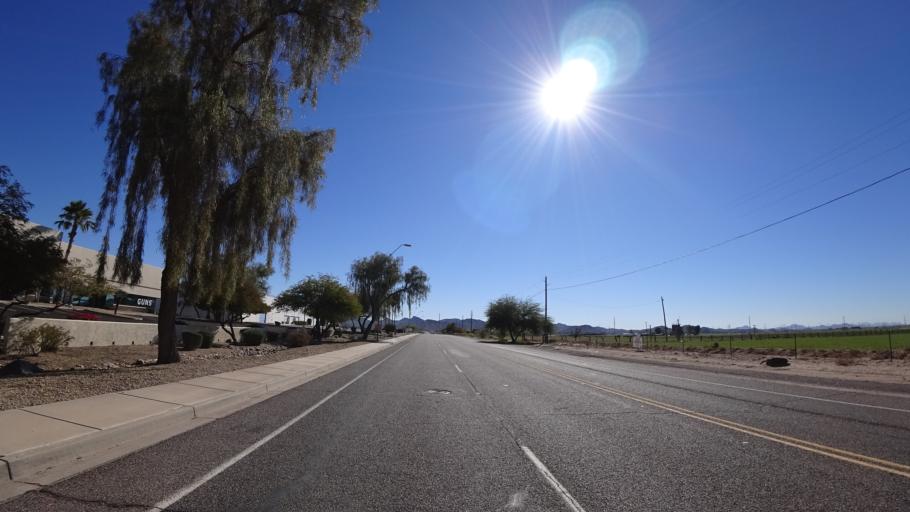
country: US
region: Arizona
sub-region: Maricopa County
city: Goodyear
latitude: 33.4125
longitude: -112.3751
